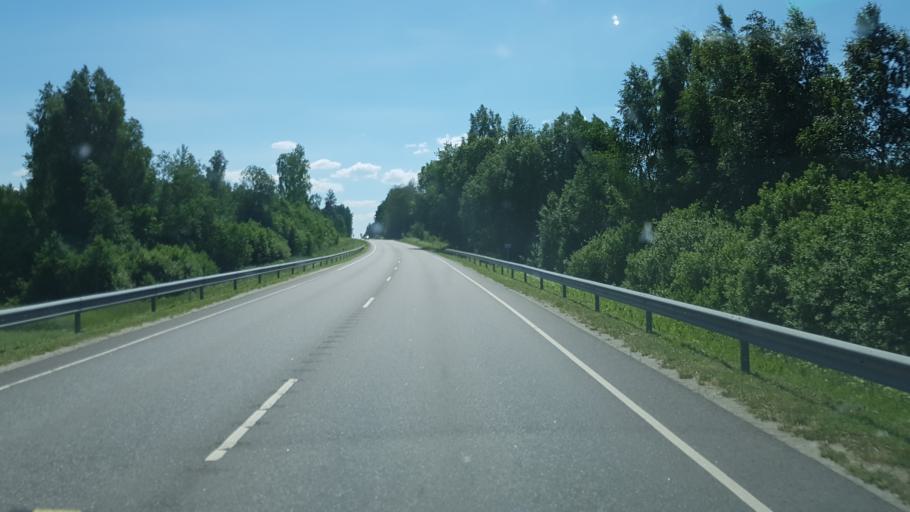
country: EE
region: Tartu
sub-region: UElenurme vald
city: Ulenurme
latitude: 58.0599
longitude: 26.7290
